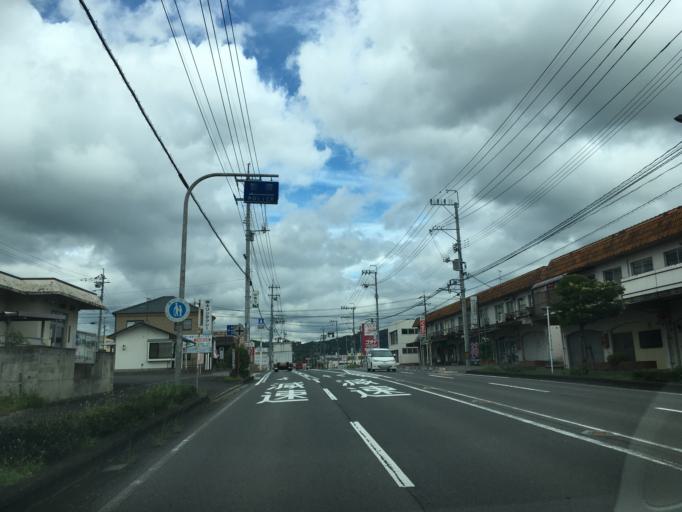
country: JP
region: Okayama
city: Okayama-shi
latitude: 34.7802
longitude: 134.0381
